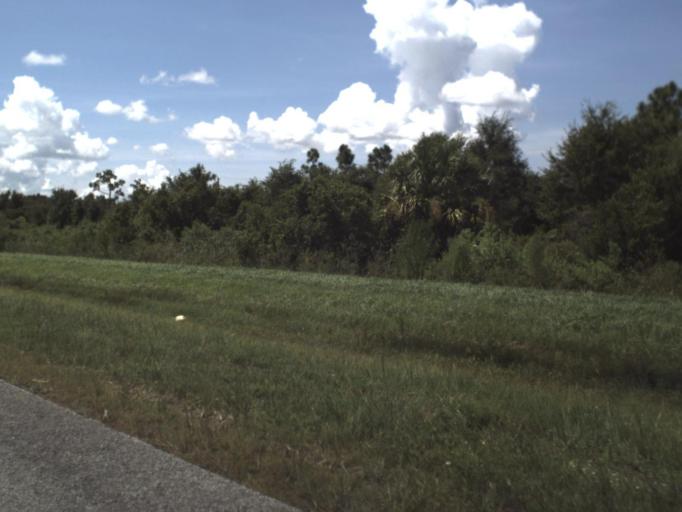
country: US
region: Florida
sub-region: Charlotte County
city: Harbour Heights
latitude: 27.0255
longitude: -81.9587
